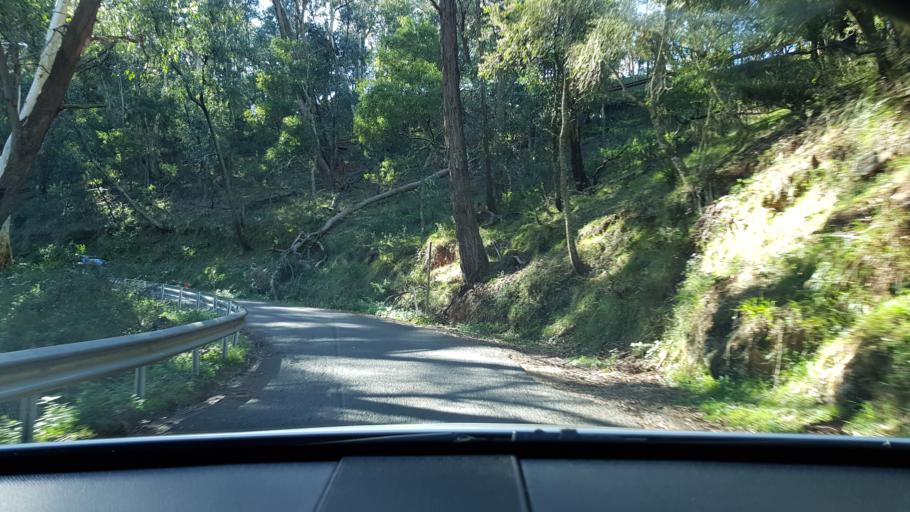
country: AU
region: New South Wales
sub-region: Oberon
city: Oberon
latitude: -33.8166
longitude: 150.0218
